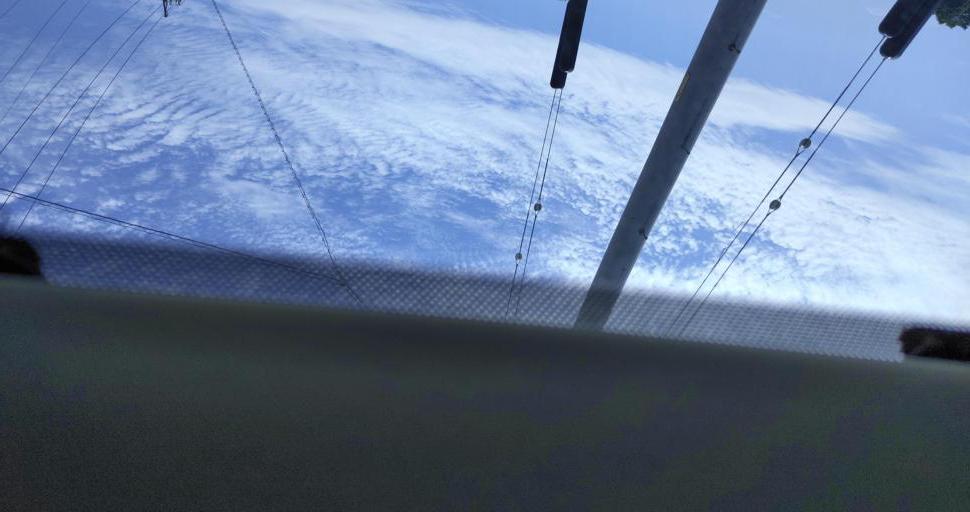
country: JP
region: Nagano
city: Ueda
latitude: 36.3782
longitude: 138.3444
